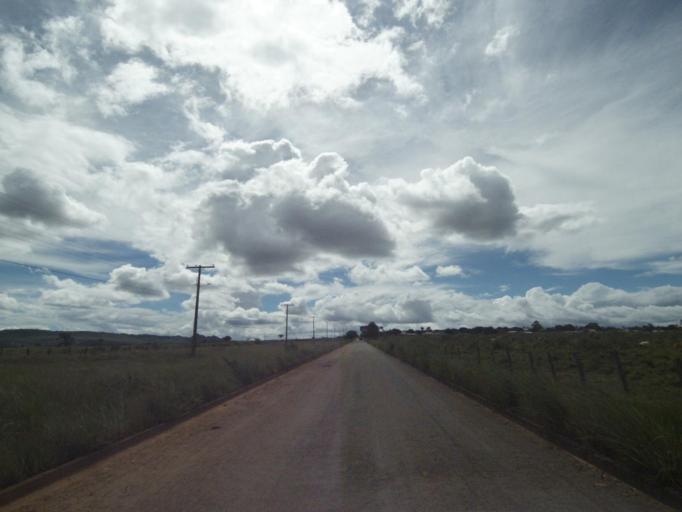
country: BR
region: Goias
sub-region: Pirenopolis
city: Pirenopolis
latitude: -15.7872
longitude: -48.7808
